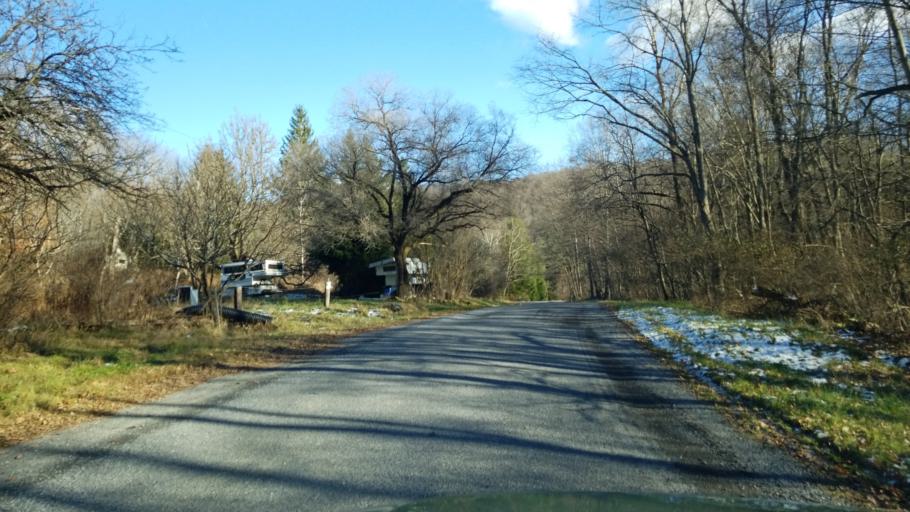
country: US
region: Pennsylvania
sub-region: Jefferson County
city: Brockway
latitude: 41.2595
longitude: -78.8003
